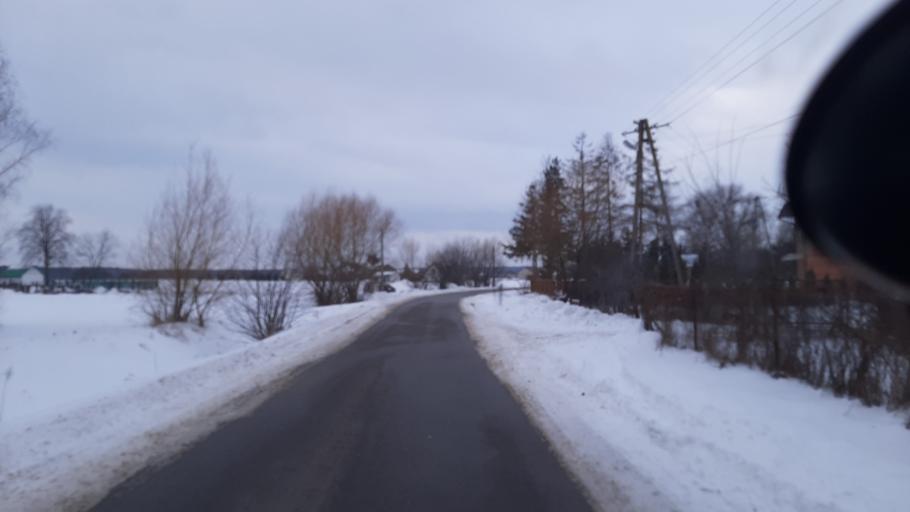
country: PL
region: Lublin Voivodeship
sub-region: Powiat lubartowski
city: Abramow
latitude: 51.4435
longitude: 22.2747
